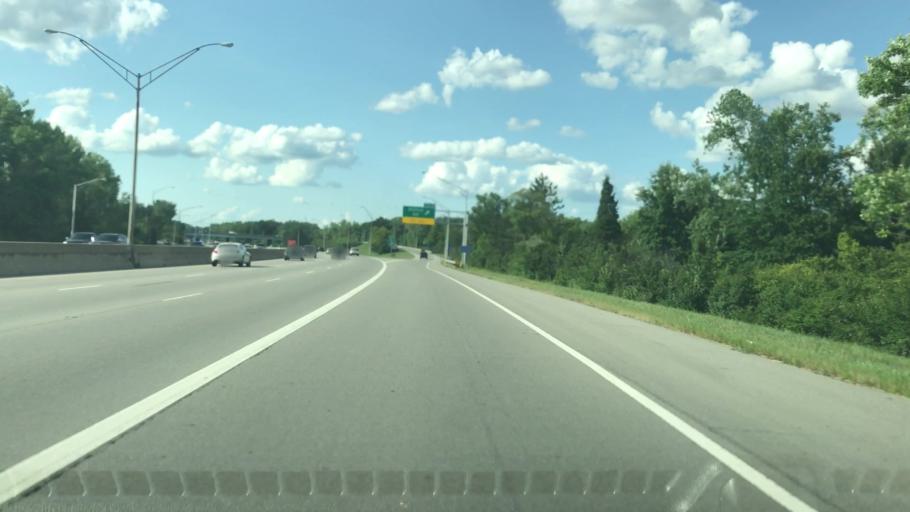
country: US
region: Ohio
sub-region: Franklin County
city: Worthington
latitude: 40.0584
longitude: -83.0304
